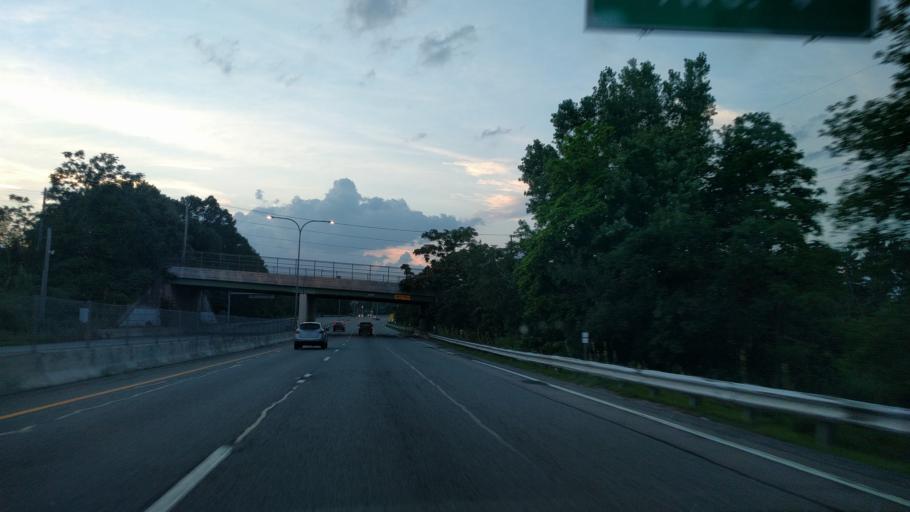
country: US
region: Rhode Island
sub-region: Providence County
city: Providence
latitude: 41.8491
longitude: -71.4236
